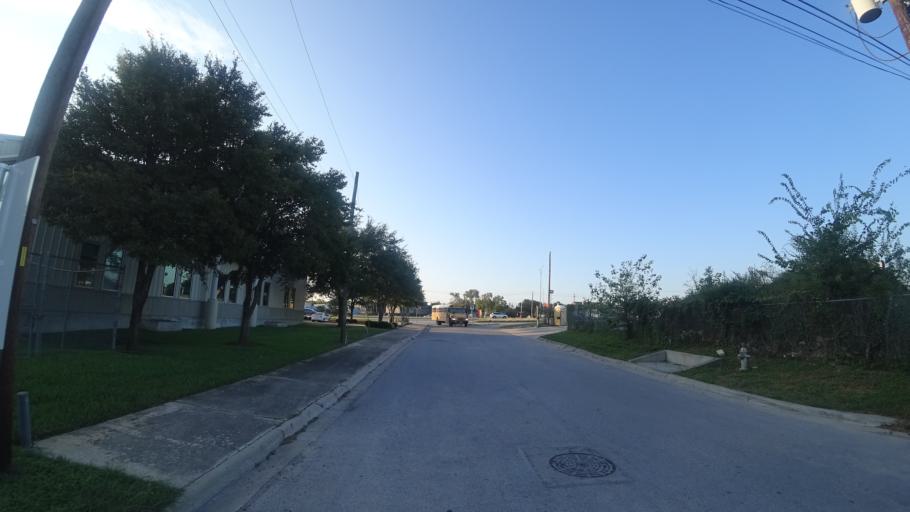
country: US
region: Texas
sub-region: Travis County
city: Austin
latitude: 30.3225
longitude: -97.6860
